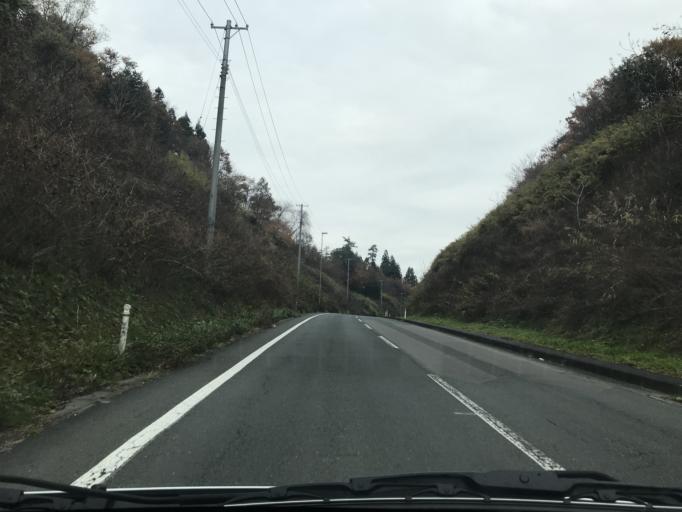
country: JP
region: Iwate
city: Mizusawa
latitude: 39.1650
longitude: 141.2042
